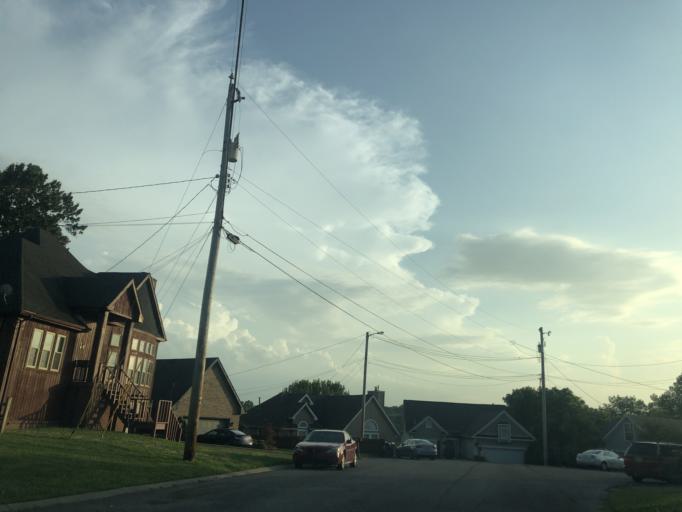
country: US
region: Tennessee
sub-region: Davidson County
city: Lakewood
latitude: 36.1358
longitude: -86.6367
